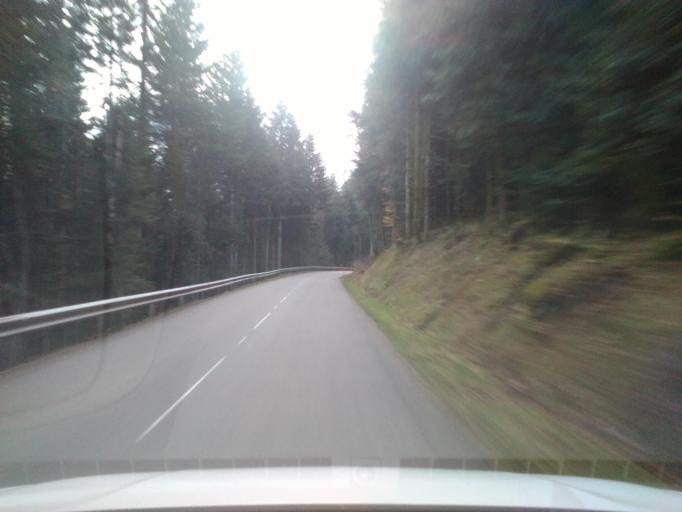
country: FR
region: Lorraine
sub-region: Departement des Vosges
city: Fraize
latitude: 48.2014
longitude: 7.0203
